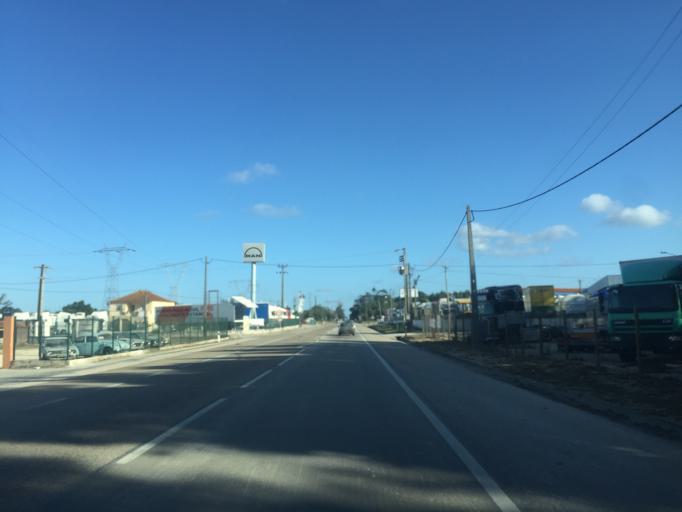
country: PT
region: Leiria
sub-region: Alcobaca
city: Turquel
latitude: 39.4625
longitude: -8.9445
